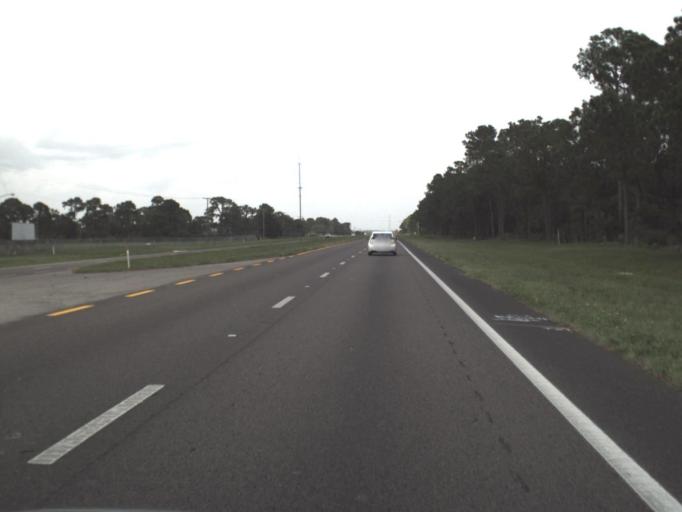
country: US
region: Florida
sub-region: Polk County
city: Crooked Lake Park
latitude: 27.7778
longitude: -81.5971
